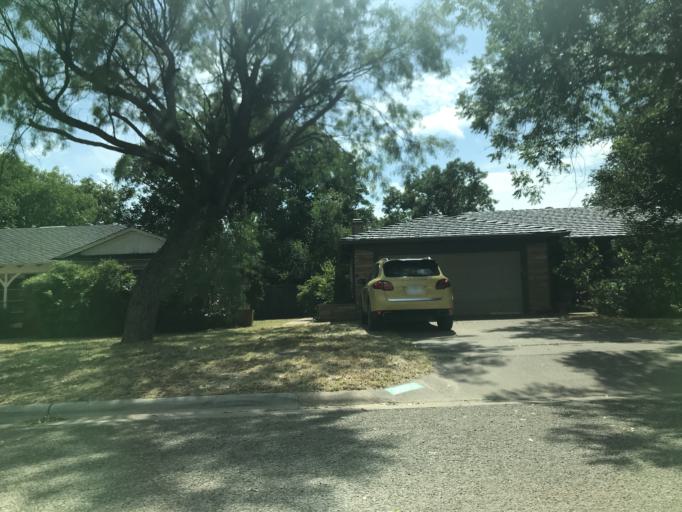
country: US
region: Texas
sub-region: Taylor County
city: Abilene
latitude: 32.4482
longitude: -99.7718
